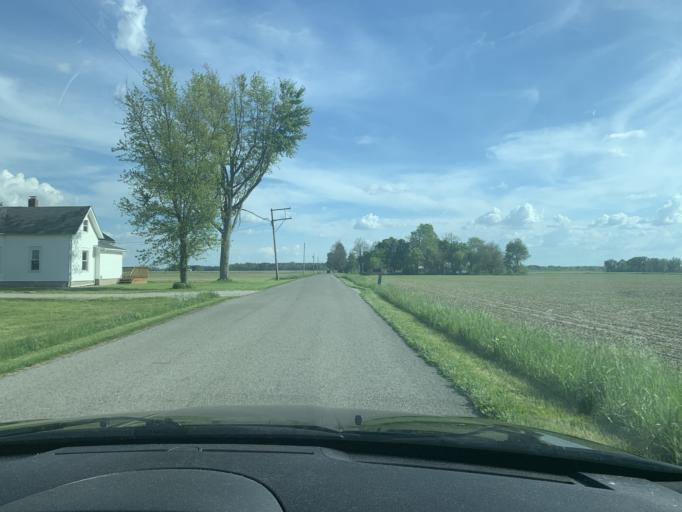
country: US
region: Ohio
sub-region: Logan County
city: De Graff
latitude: 40.2554
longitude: -84.0166
